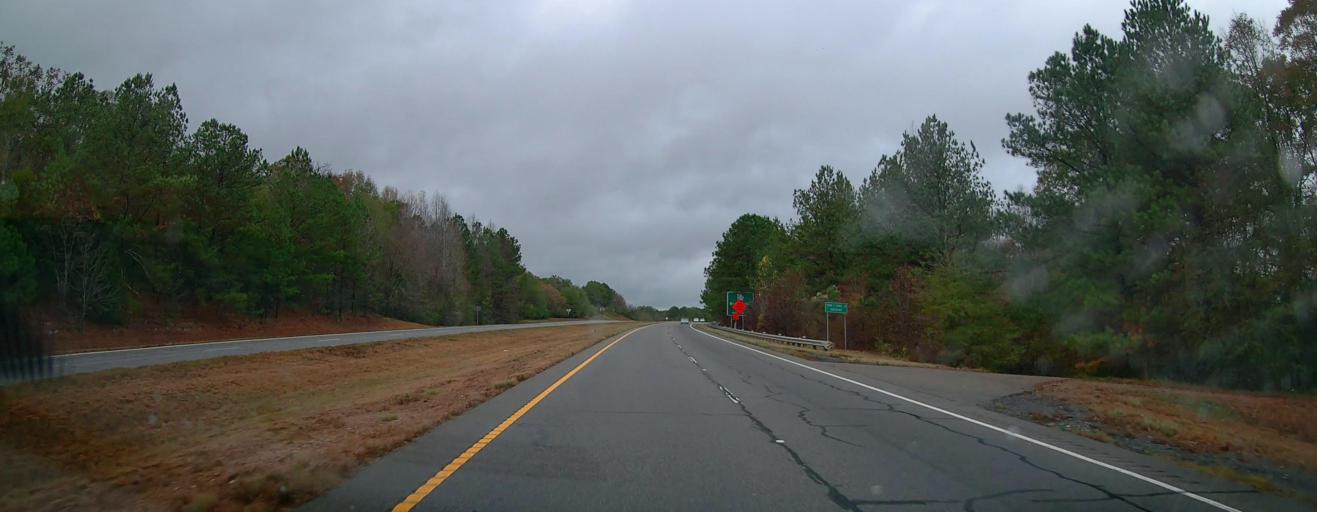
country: US
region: Georgia
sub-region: Oconee County
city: Watkinsville
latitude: 33.8628
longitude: -83.4247
